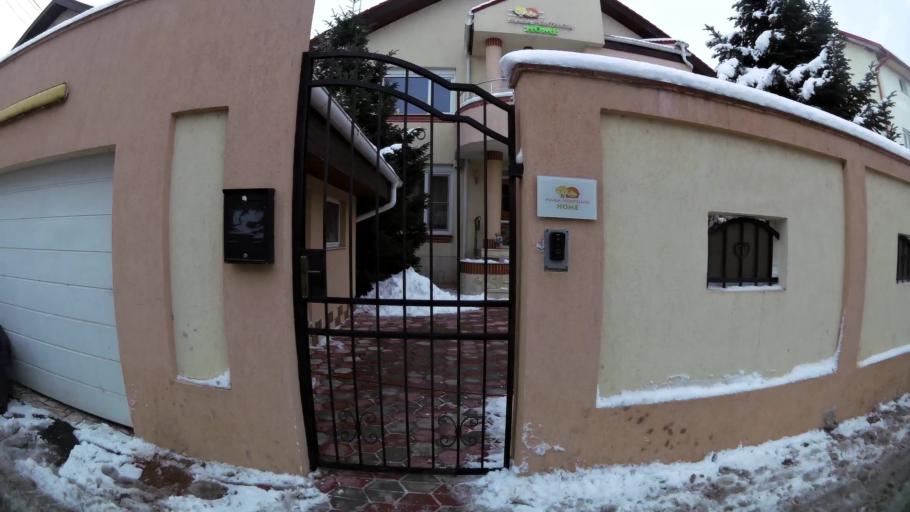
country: RO
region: Ilfov
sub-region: Voluntari City
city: Voluntari
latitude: 44.5096
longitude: 26.1417
